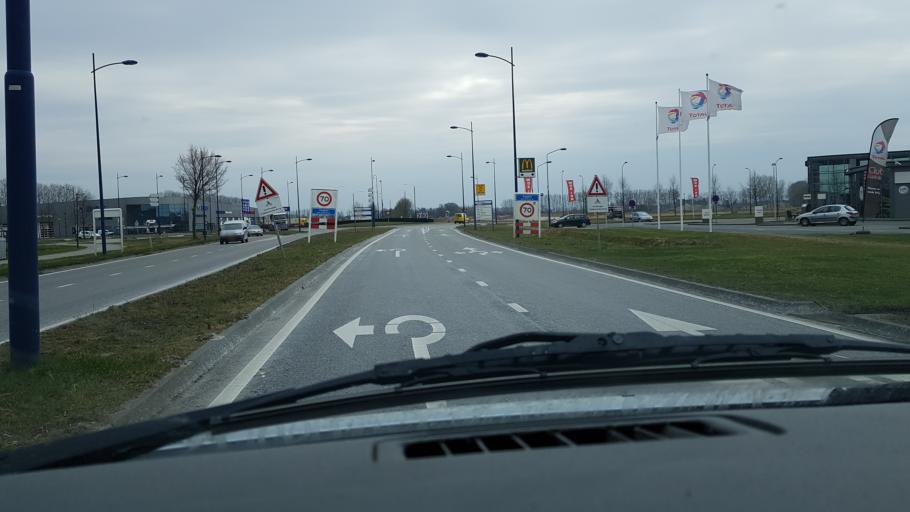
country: NL
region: North Brabant
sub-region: Gemeente Veghel
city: Eerde
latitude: 51.6000
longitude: 5.5164
